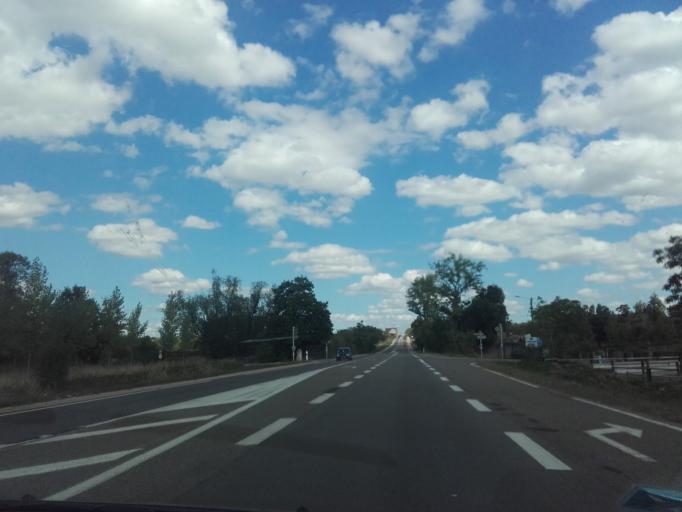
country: FR
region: Bourgogne
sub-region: Departement de Saone-et-Loire
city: La Chapelle-de-Guinchay
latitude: 46.1972
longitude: 4.7631
